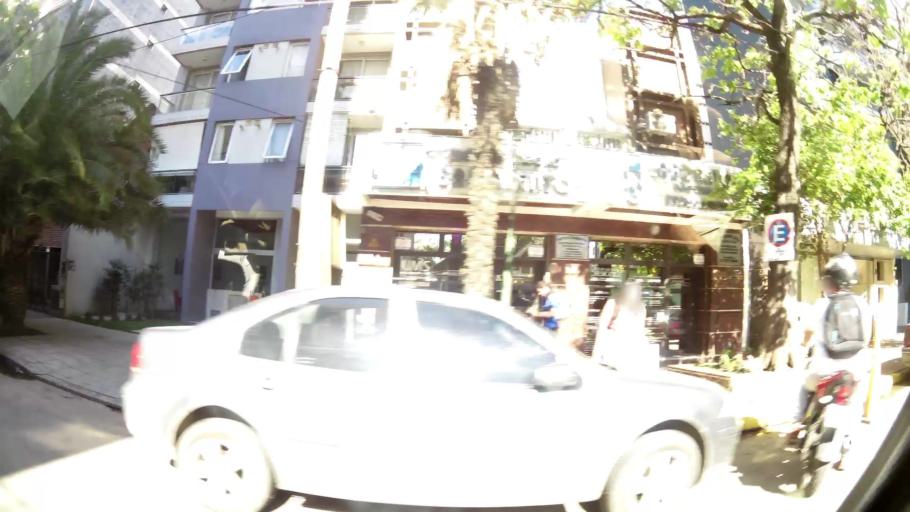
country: AR
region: Buenos Aires
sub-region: Partido de Lomas de Zamora
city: Lomas de Zamora
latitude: -34.7632
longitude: -58.4047
